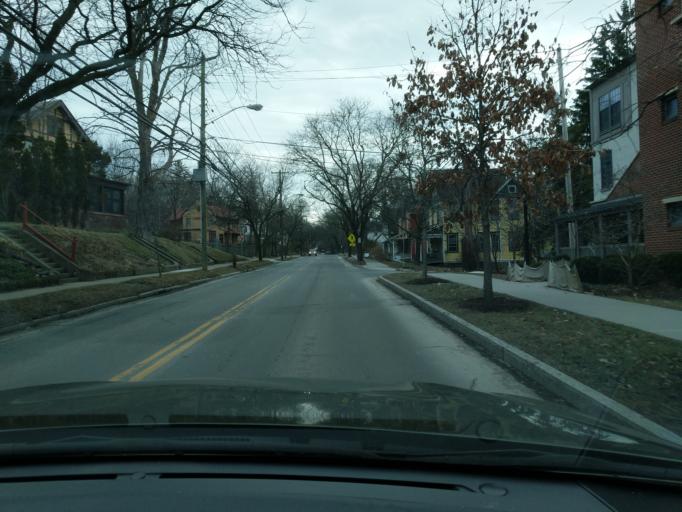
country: US
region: New York
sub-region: Tompkins County
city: East Ithaca
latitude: 42.4368
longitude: -76.4856
